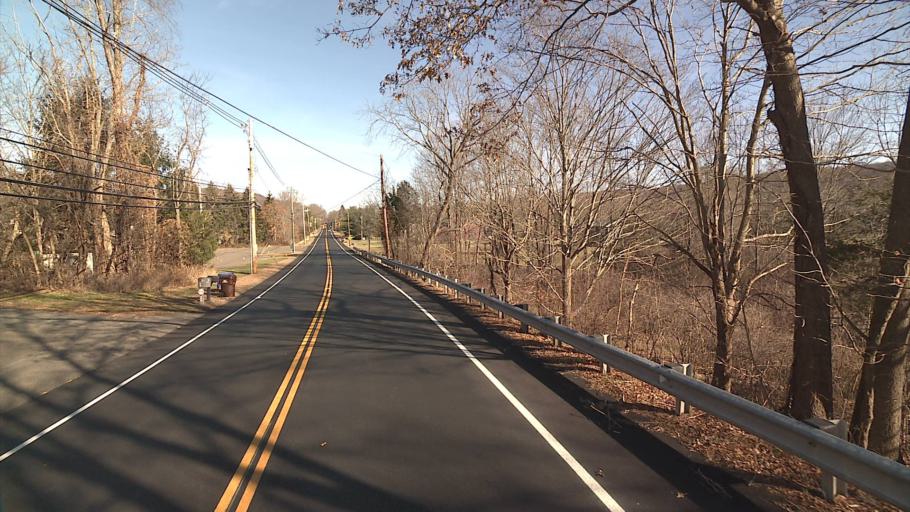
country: US
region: Connecticut
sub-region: New Haven County
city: Wallingford Center
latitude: 41.4155
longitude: -72.7473
